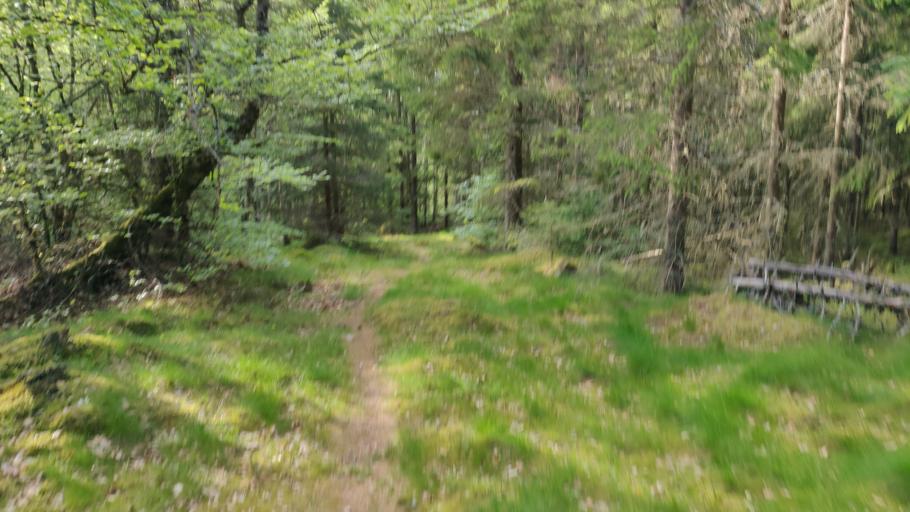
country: SE
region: Vaestra Goetaland
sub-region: Ulricehamns Kommun
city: Ulricehamn
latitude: 57.7842
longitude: 13.3751
